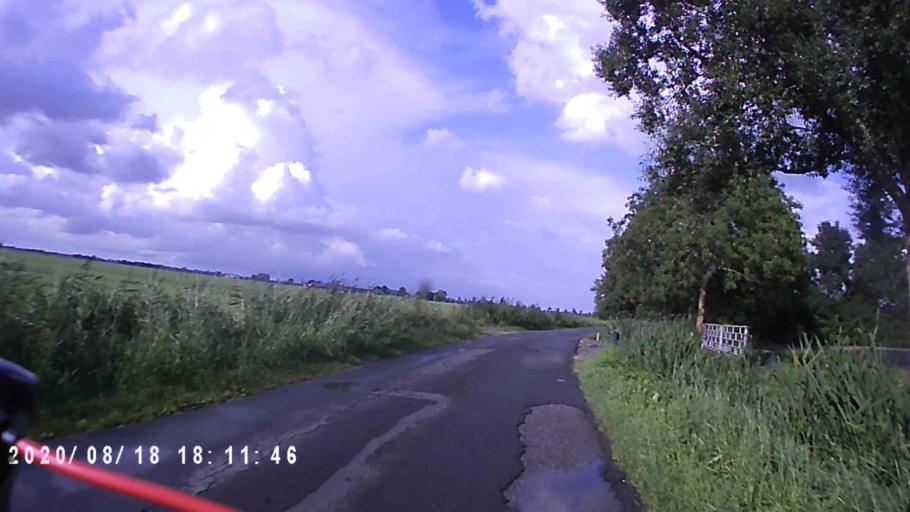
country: NL
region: Groningen
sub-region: Gemeente Zuidhorn
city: Oldehove
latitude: 53.2848
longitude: 6.4156
